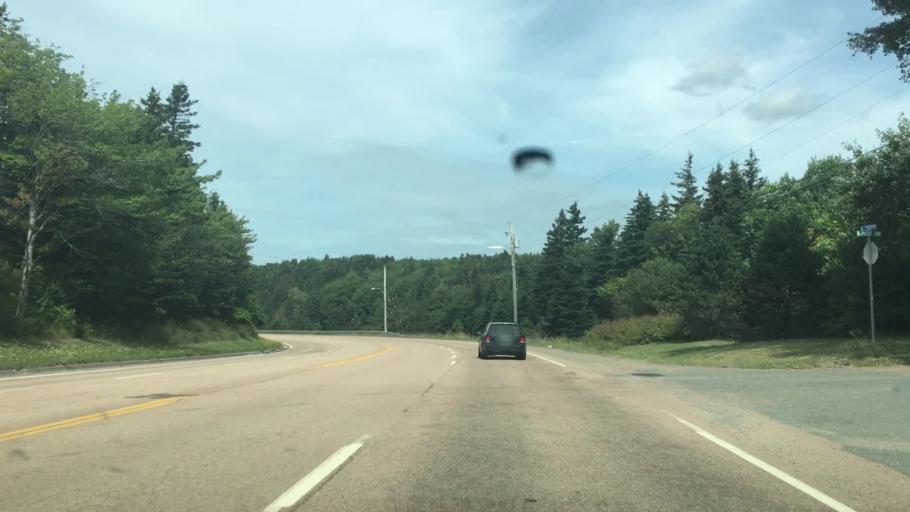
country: CA
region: Nova Scotia
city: Port Hawkesbury
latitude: 45.6237
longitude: -61.3652
